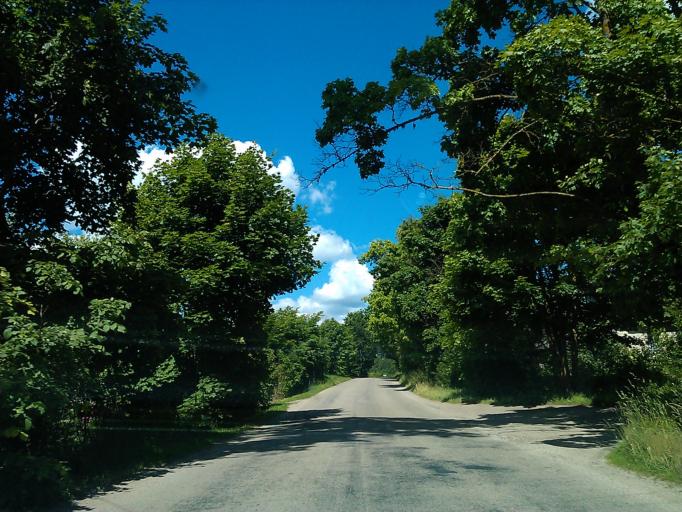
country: LV
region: Vilanu
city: Vilani
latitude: 56.5682
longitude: 26.9309
